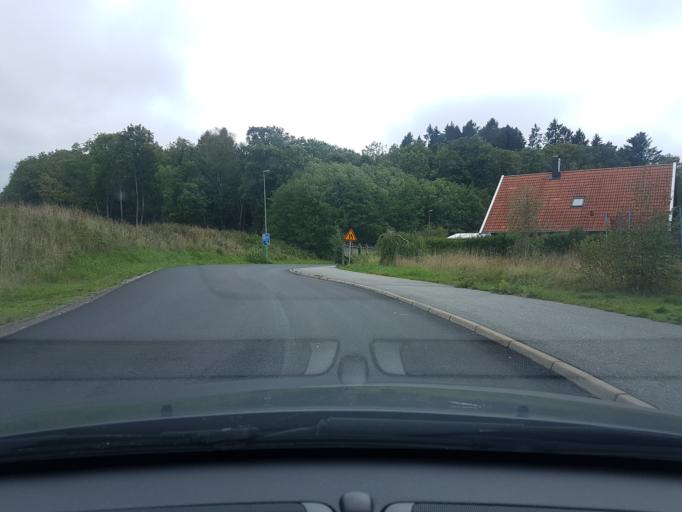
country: SE
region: Vaestra Goetaland
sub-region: Ale Kommun
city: Nodinge-Nol
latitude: 57.8853
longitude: 12.0503
